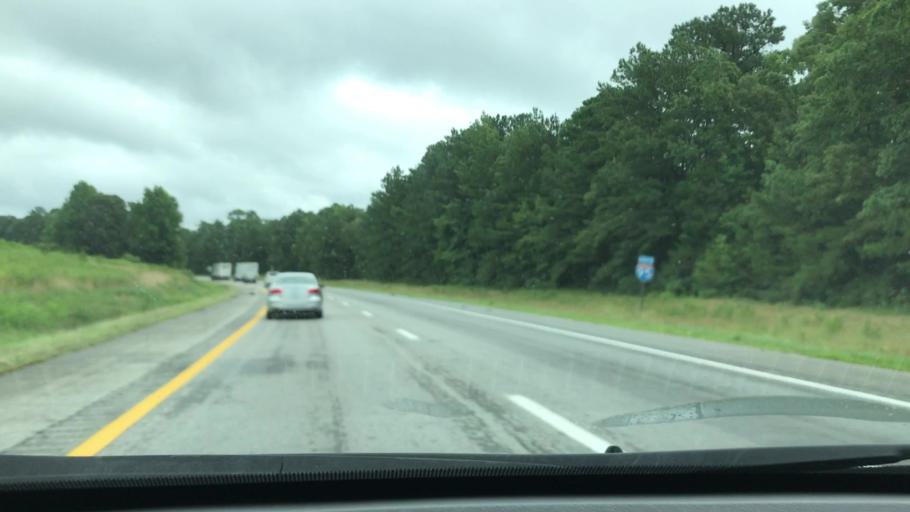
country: US
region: Virginia
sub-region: City of Emporia
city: Emporia
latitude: 36.7700
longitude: -77.4651
